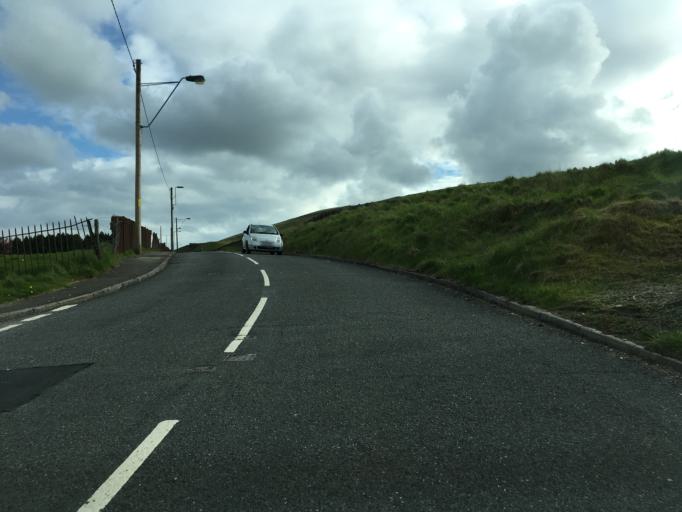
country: GB
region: Wales
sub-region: Caerphilly County Borough
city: Rhymney
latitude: 51.7398
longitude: -3.2990
